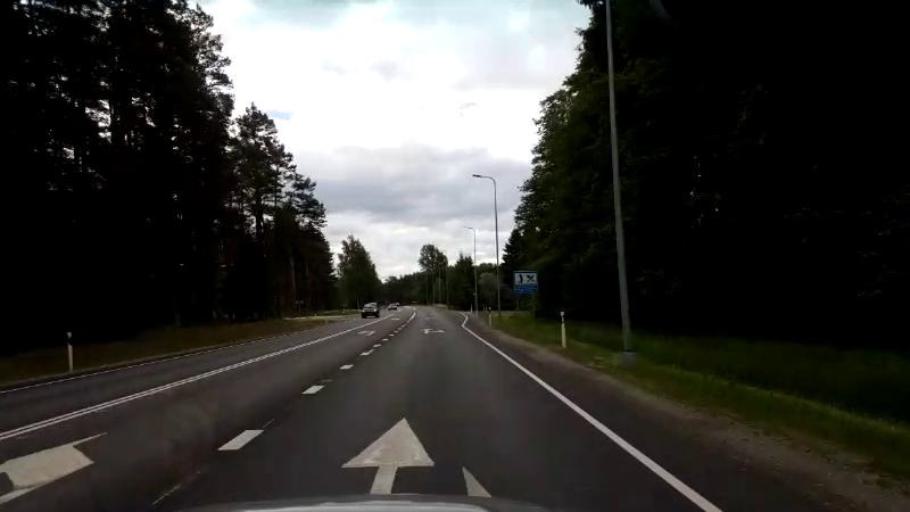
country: EE
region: Paernumaa
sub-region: Paikuse vald
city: Paikuse
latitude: 58.3210
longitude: 24.5984
